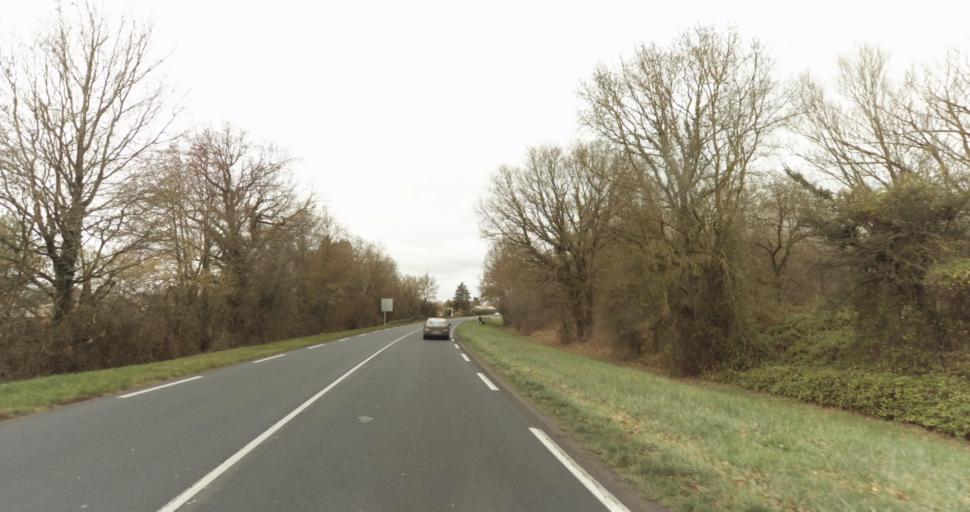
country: FR
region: Pays de la Loire
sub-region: Departement de Maine-et-Loire
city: Jumelles
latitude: 47.3833
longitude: -0.1105
